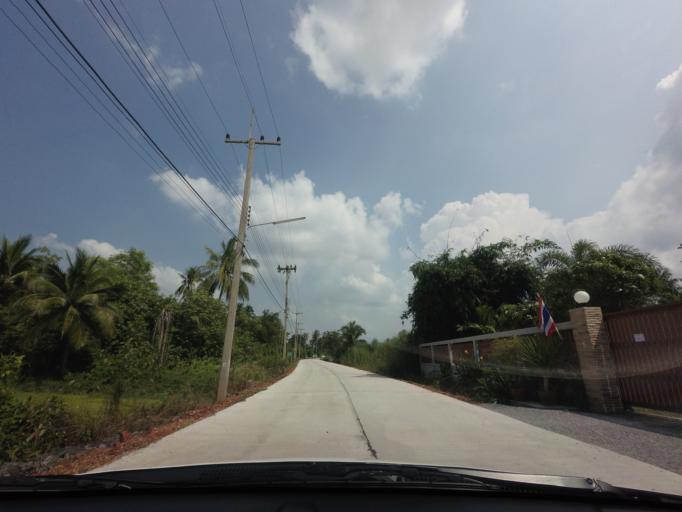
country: TH
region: Nakhon Pathom
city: Nakhon Chai Si
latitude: 13.8152
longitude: 100.1945
